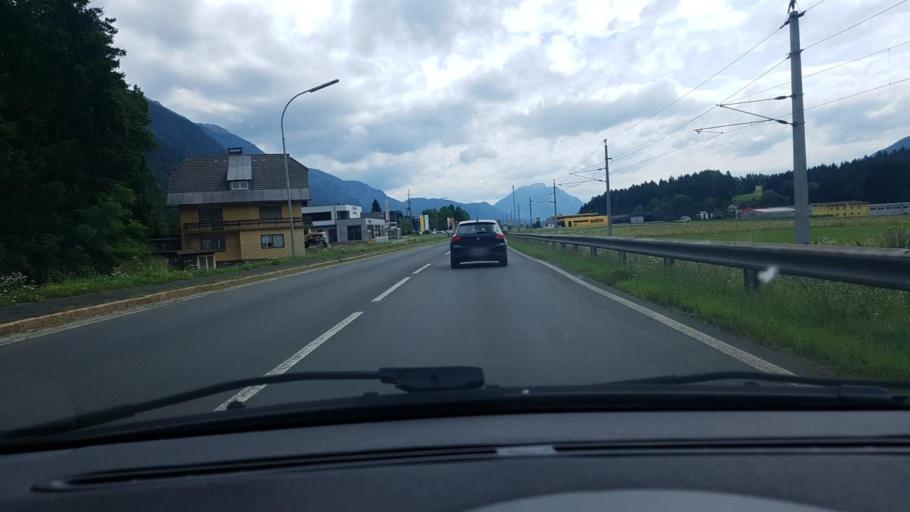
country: AT
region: Carinthia
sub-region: Politischer Bezirk Hermagor
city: Hermagor
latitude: 46.6312
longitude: 13.3874
